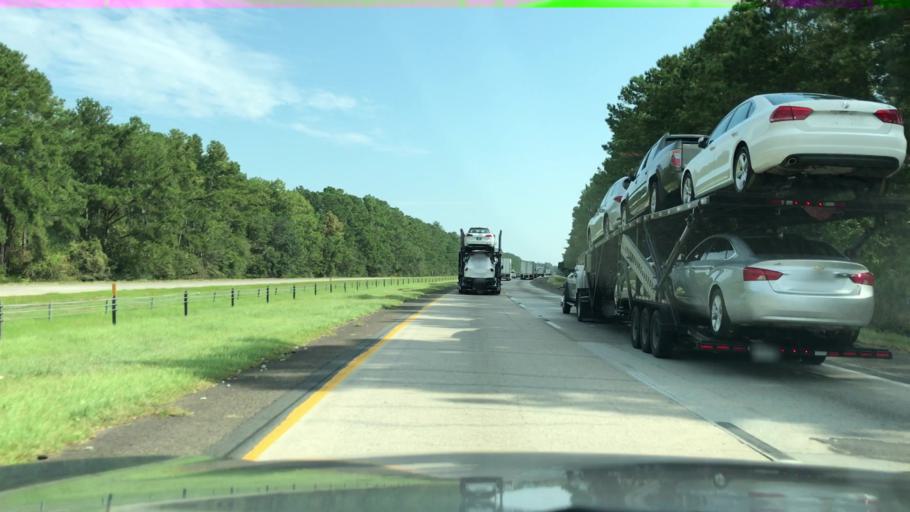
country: US
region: South Carolina
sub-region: Colleton County
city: Walterboro
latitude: 32.8095
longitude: -80.7668
